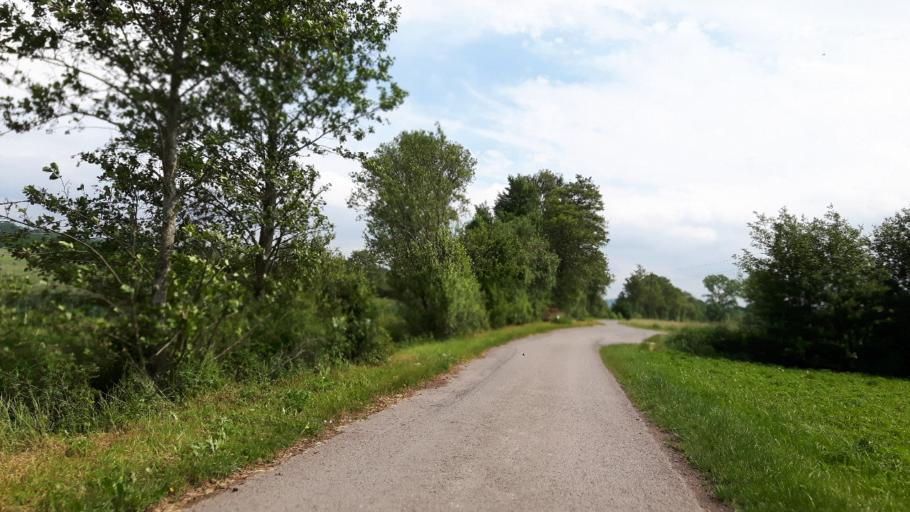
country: DE
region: Bavaria
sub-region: Regierungsbezirk Unterfranken
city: Herbstadt
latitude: 50.3062
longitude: 10.5084
